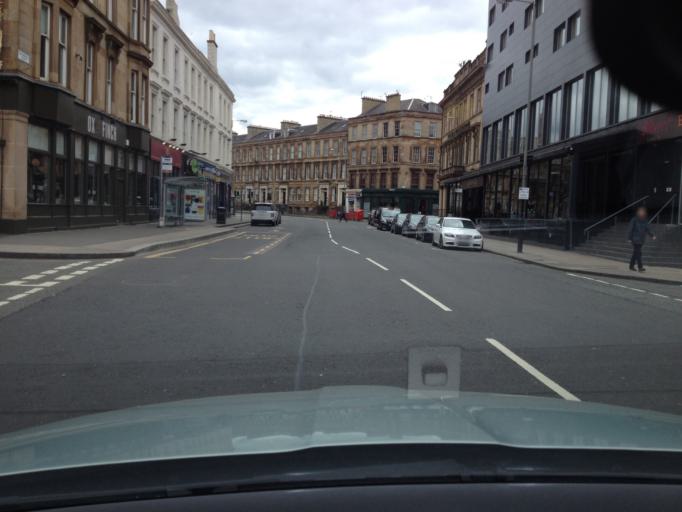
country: GB
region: Scotland
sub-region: Glasgow City
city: Glasgow
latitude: 55.8658
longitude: -4.2851
